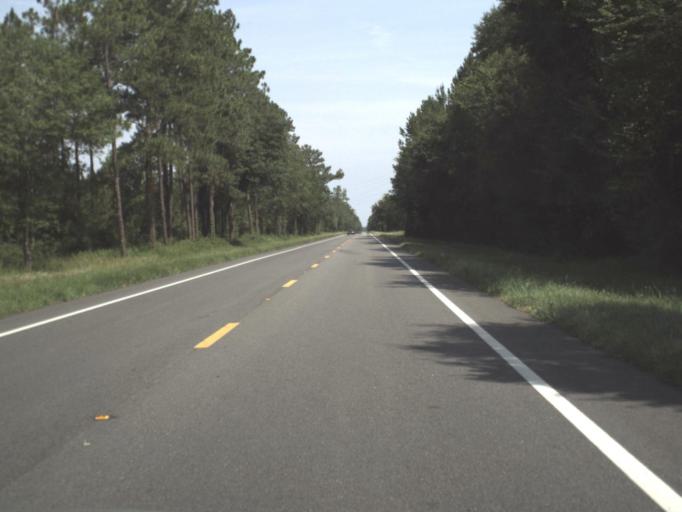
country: US
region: Florida
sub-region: Hamilton County
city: Jasper
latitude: 30.5784
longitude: -82.9971
